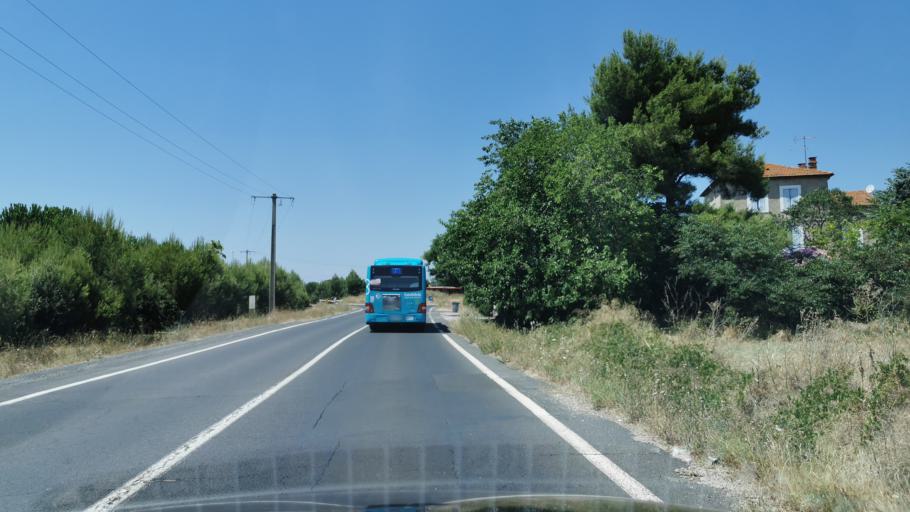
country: FR
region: Languedoc-Roussillon
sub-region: Departement de l'Herault
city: Beziers
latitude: 43.3415
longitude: 3.1809
